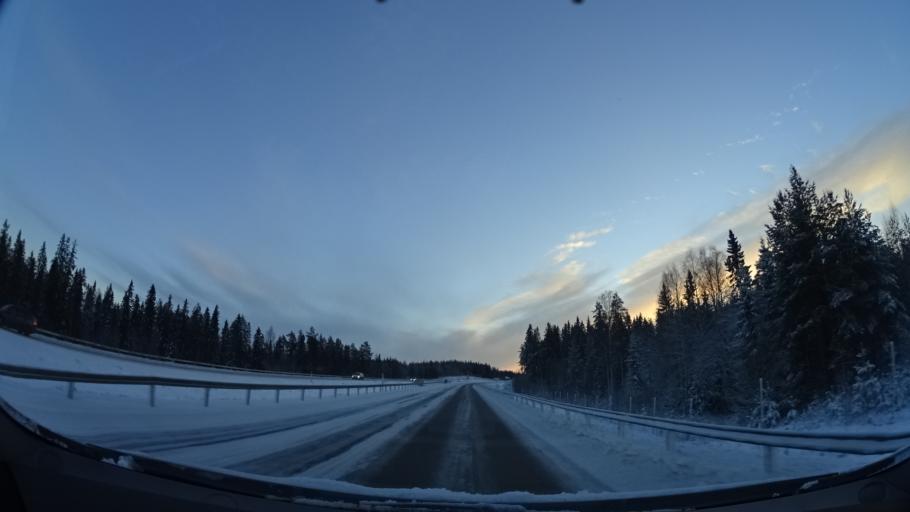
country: SE
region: Vaesterbotten
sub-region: Skelleftea Kommun
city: Kage
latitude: 64.7791
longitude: 21.0197
